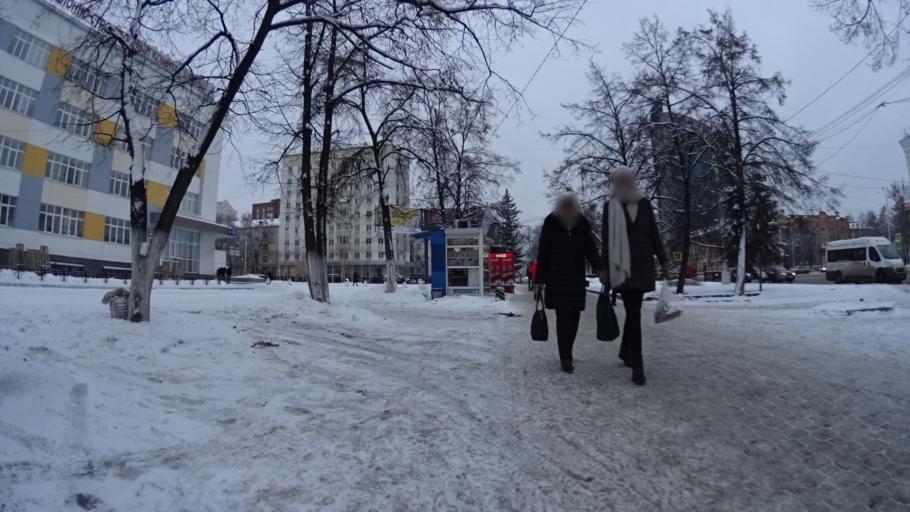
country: RU
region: Bashkortostan
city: Ufa
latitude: 54.7353
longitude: 55.9529
